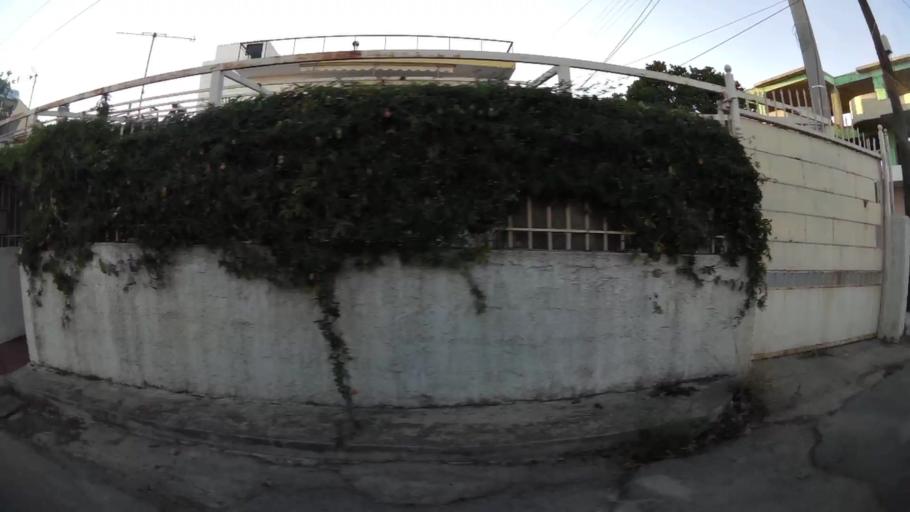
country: GR
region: Attica
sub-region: Nomarchia Dytikis Attikis
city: Ano Liosia
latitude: 38.0874
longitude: 23.6900
